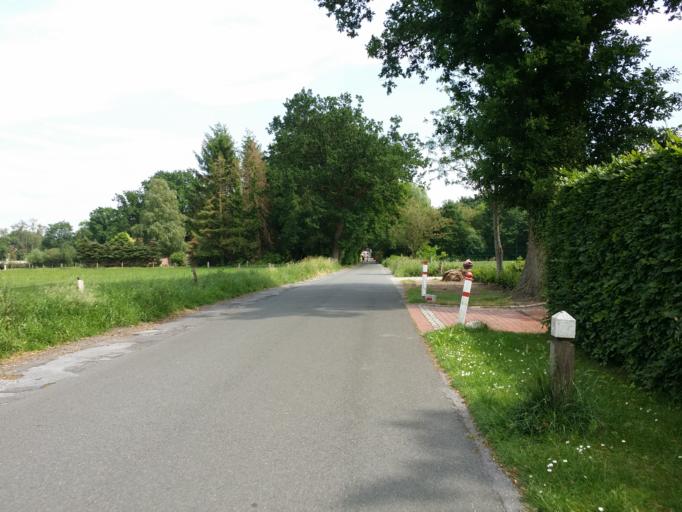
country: DE
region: Lower Saxony
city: Rastede
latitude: 53.2019
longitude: 8.1982
